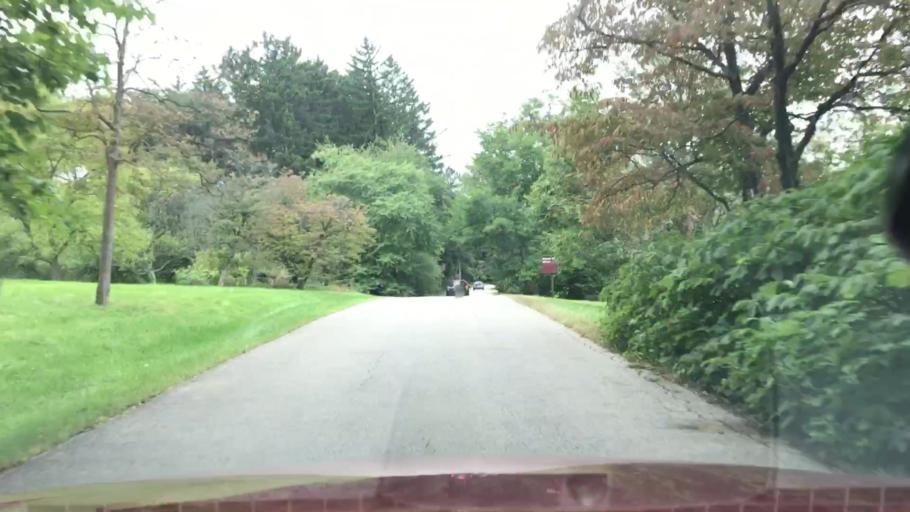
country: US
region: Illinois
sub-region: DuPage County
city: Lisle
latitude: 41.8185
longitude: -88.0632
